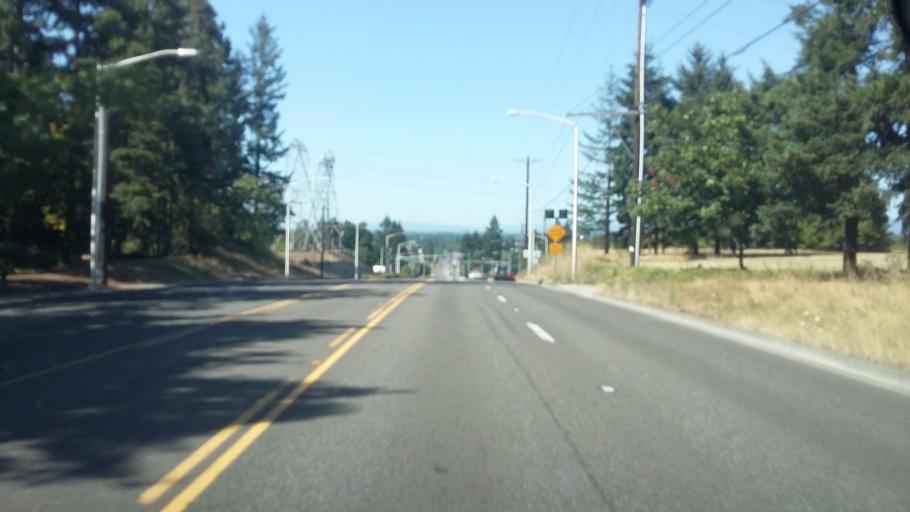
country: US
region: Washington
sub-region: Clark County
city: Orchards
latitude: 45.6334
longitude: -122.5579
